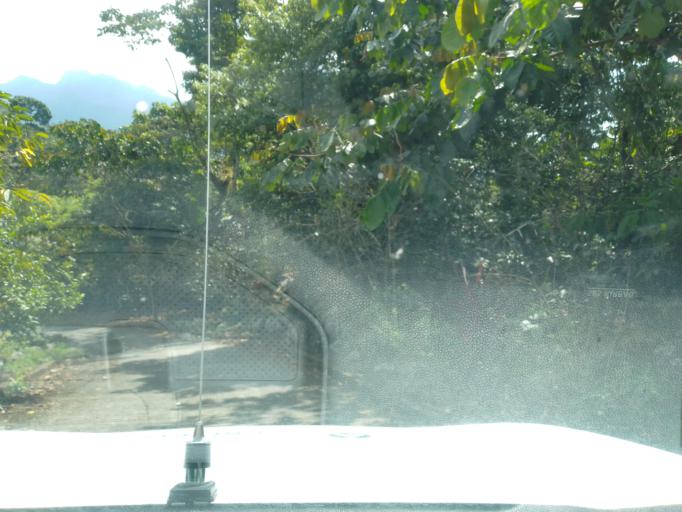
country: MX
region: Chiapas
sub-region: Union Juarez
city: Santo Domingo
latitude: 15.0732
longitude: -92.0940
